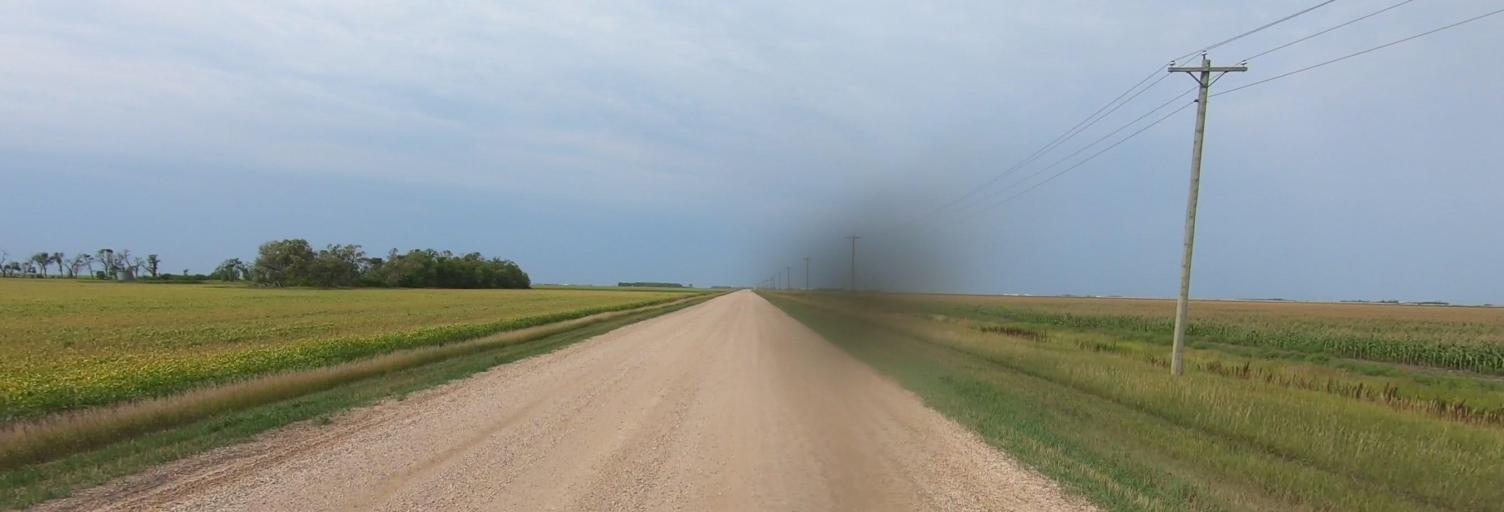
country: CA
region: Manitoba
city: Morris
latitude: 49.5764
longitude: -97.2826
